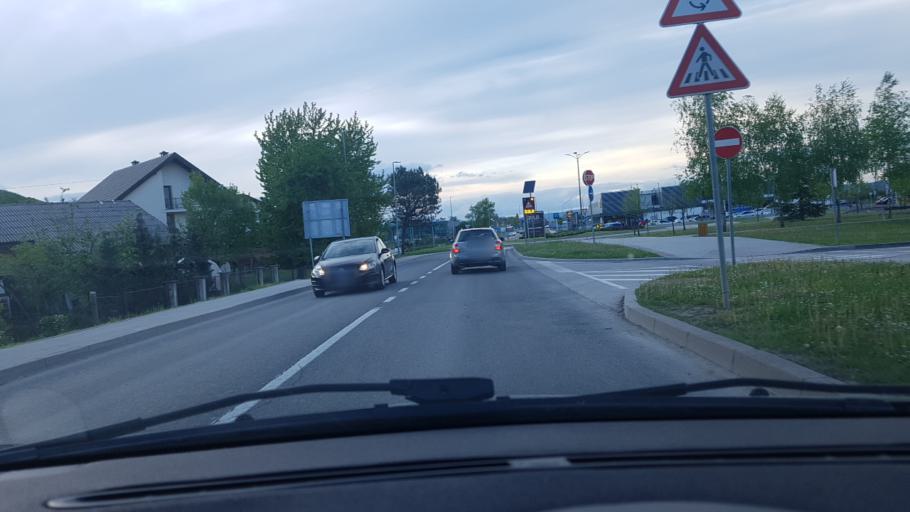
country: HR
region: Zagrebacka
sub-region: Grad Samobor
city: Samobor
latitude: 45.8079
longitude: 15.7158
